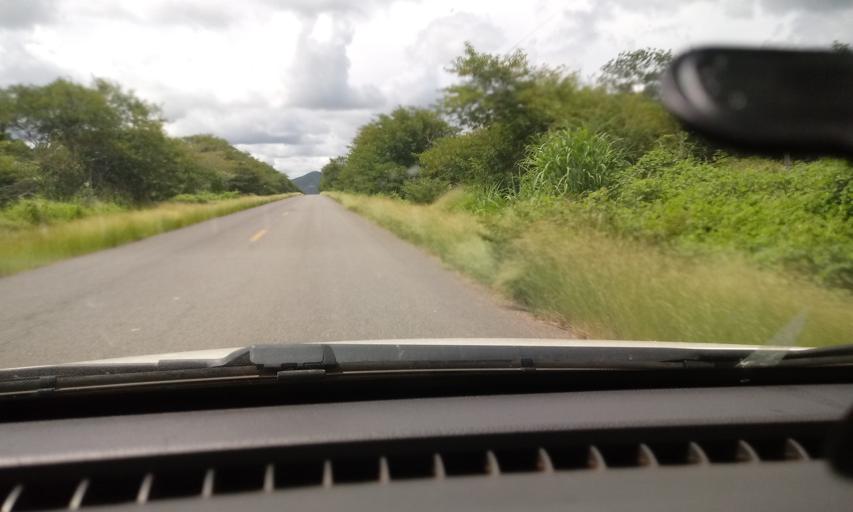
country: BR
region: Bahia
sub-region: Guanambi
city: Guanambi
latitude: -13.9303
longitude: -42.8480
